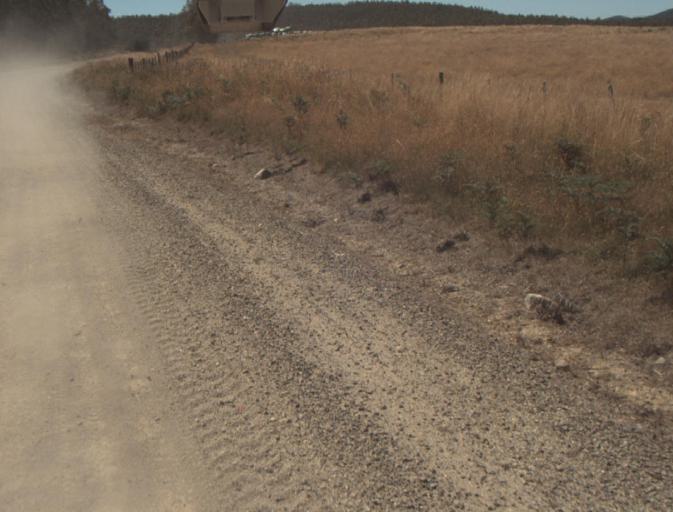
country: AU
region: Tasmania
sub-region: Dorset
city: Scottsdale
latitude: -41.3258
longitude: 147.4447
